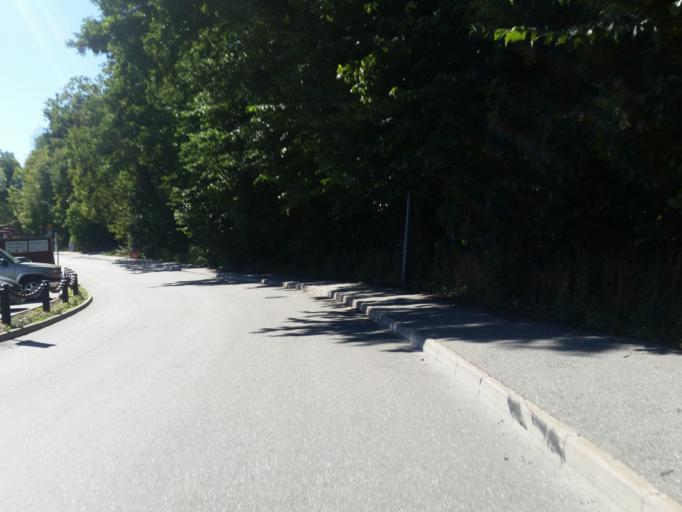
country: SE
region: Stockholm
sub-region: Solna Kommun
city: Solna
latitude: 59.3449
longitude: 18.0065
